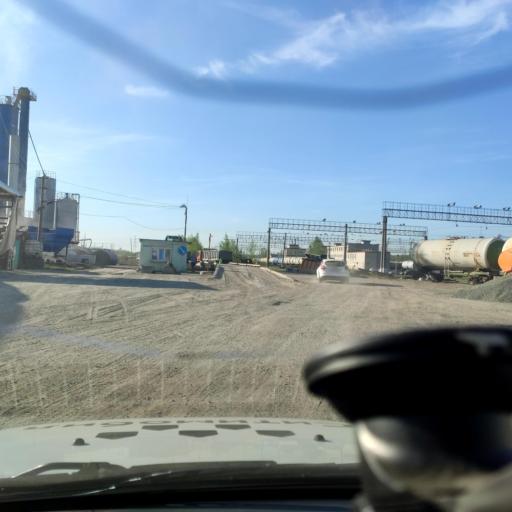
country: RU
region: Perm
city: Gamovo
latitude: 57.9062
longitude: 56.1789
